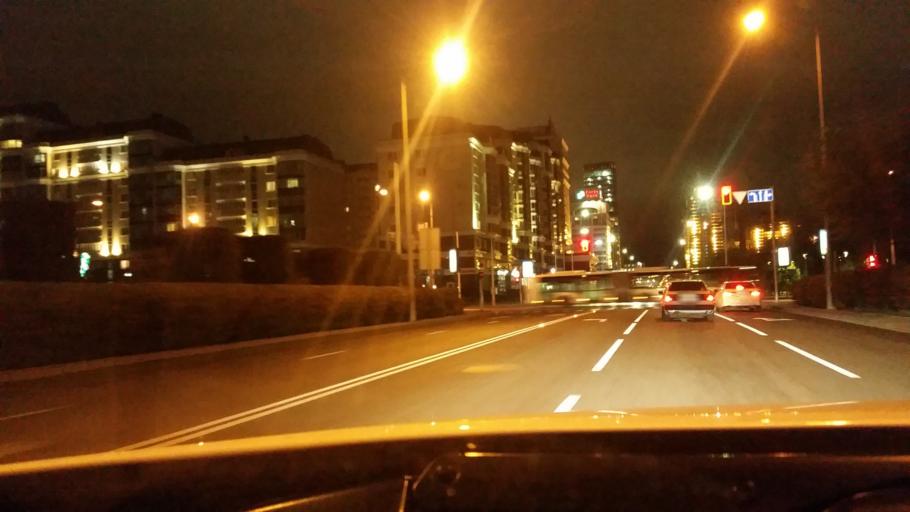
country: KZ
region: Astana Qalasy
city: Astana
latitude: 51.1310
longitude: 71.4334
